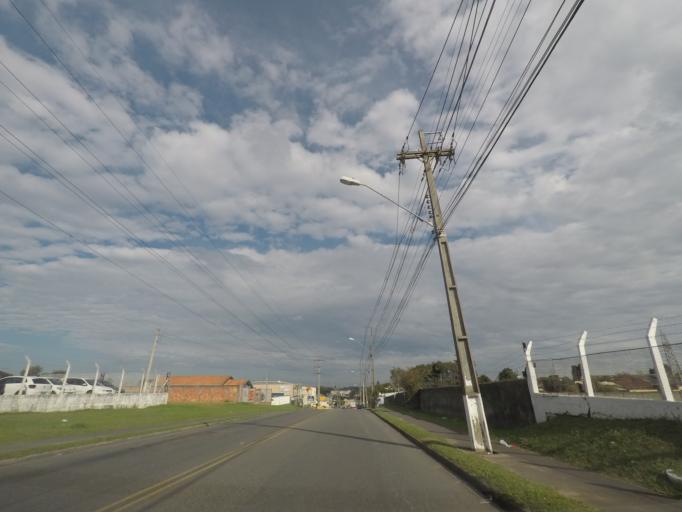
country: BR
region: Parana
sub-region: Sao Jose Dos Pinhais
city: Sao Jose dos Pinhais
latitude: -25.5487
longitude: -49.2932
